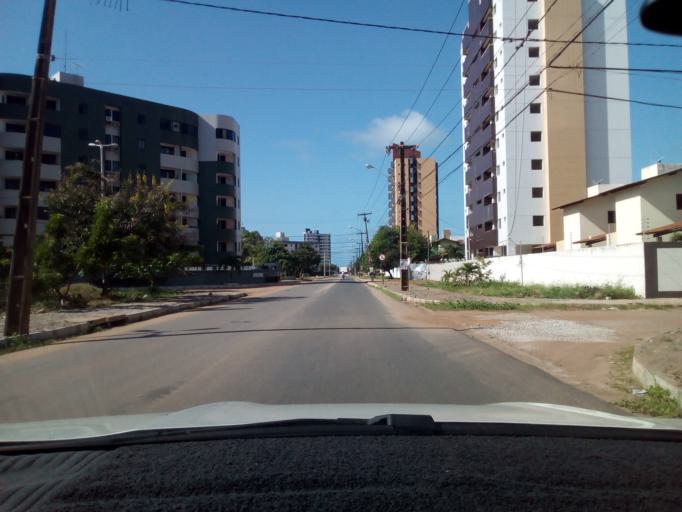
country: BR
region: Paraiba
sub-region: Cabedelo
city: Cabedelo
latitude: -7.0410
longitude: -34.8434
